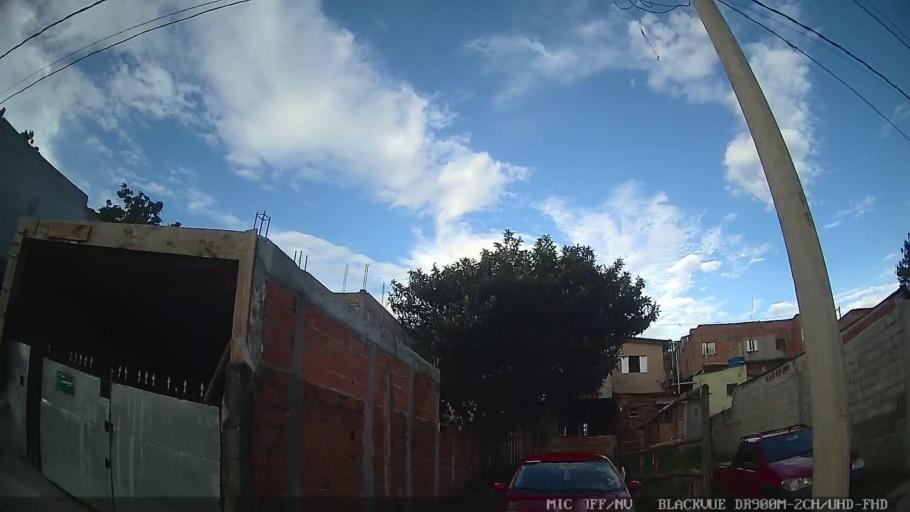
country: BR
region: Sao Paulo
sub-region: Mogi das Cruzes
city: Mogi das Cruzes
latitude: -23.5581
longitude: -46.2059
